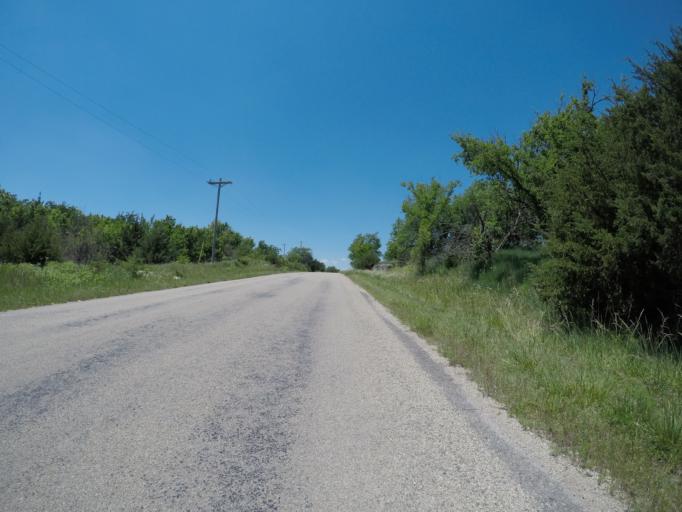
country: US
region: Kansas
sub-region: Geary County
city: Grandview Plaza
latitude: 38.8682
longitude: -96.7964
